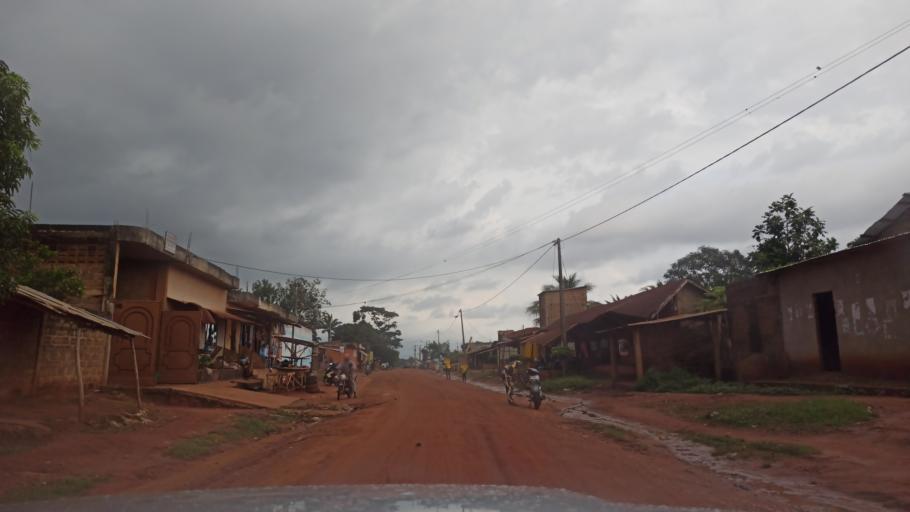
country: BJ
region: Queme
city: Porto-Novo
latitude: 6.5610
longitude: 2.5859
